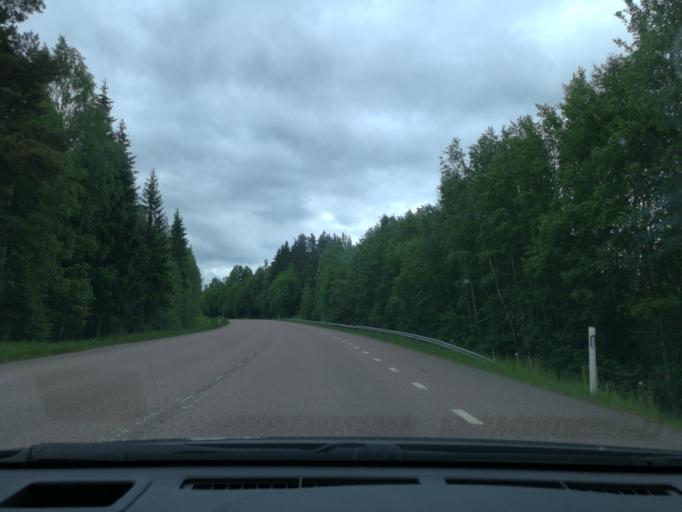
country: SE
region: Dalarna
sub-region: Ludvika Kommun
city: Ludvika
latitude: 60.1409
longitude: 15.3002
